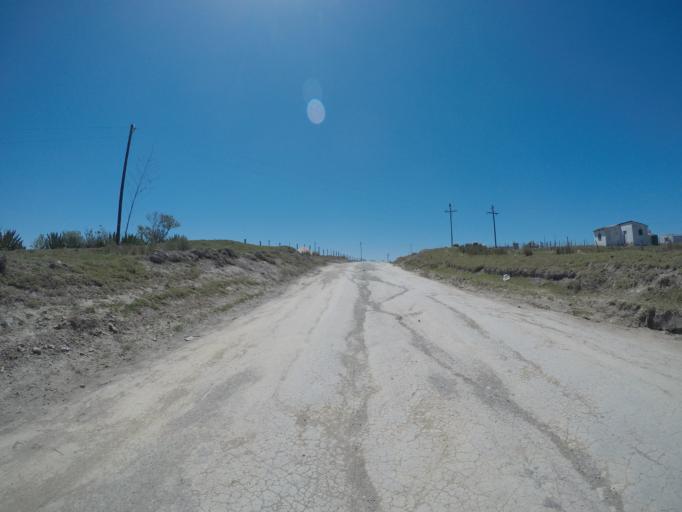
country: ZA
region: Eastern Cape
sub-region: OR Tambo District Municipality
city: Libode
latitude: -31.9398
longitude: 29.0275
